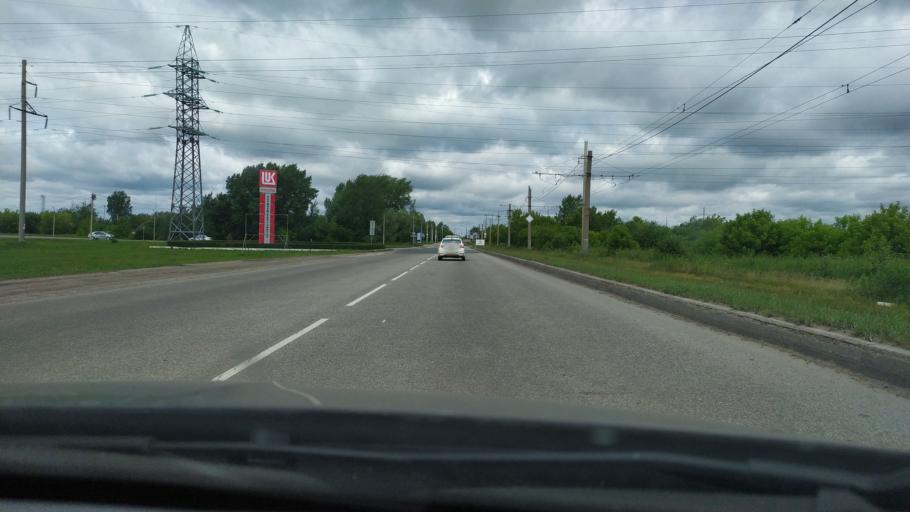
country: RU
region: Perm
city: Kondratovo
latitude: 57.9312
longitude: 56.1275
